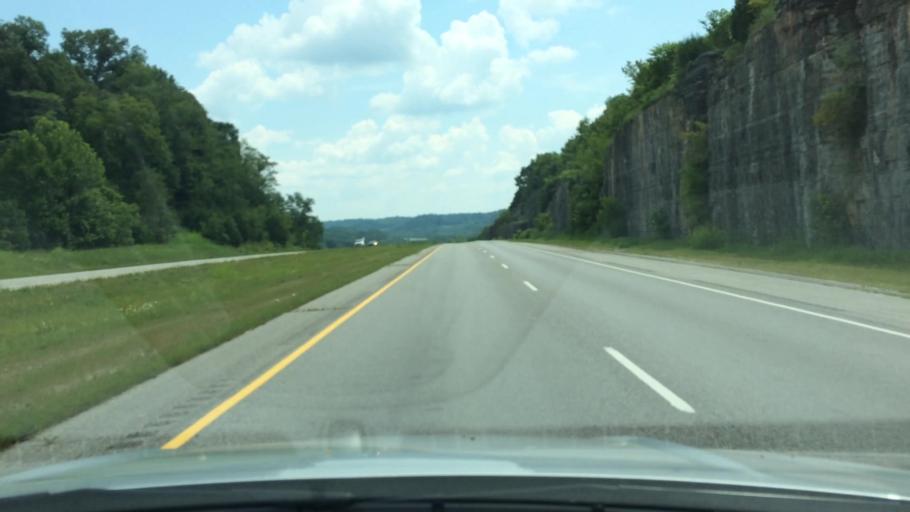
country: US
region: Tennessee
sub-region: Giles County
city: Pulaski
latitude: 35.1781
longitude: -86.9489
